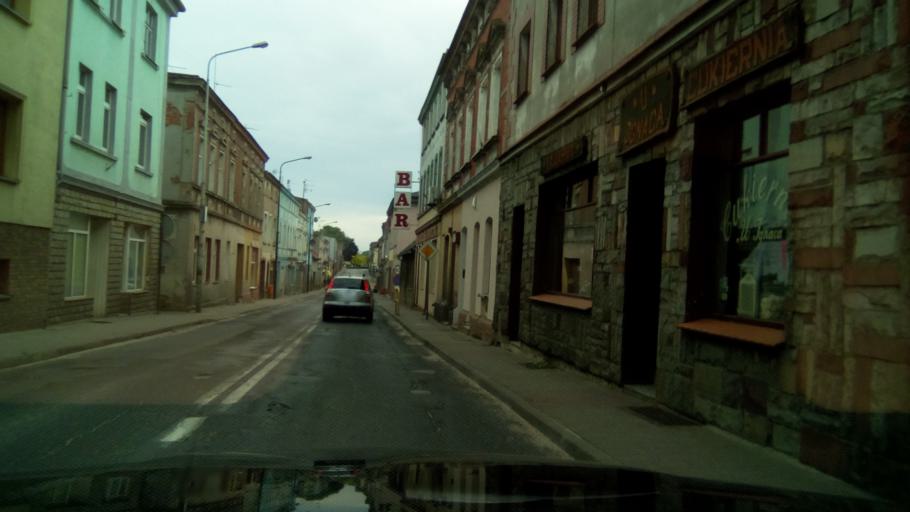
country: PL
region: Kujawsko-Pomorskie
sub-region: Powiat sepolenski
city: Wiecbork
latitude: 53.3490
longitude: 17.4858
